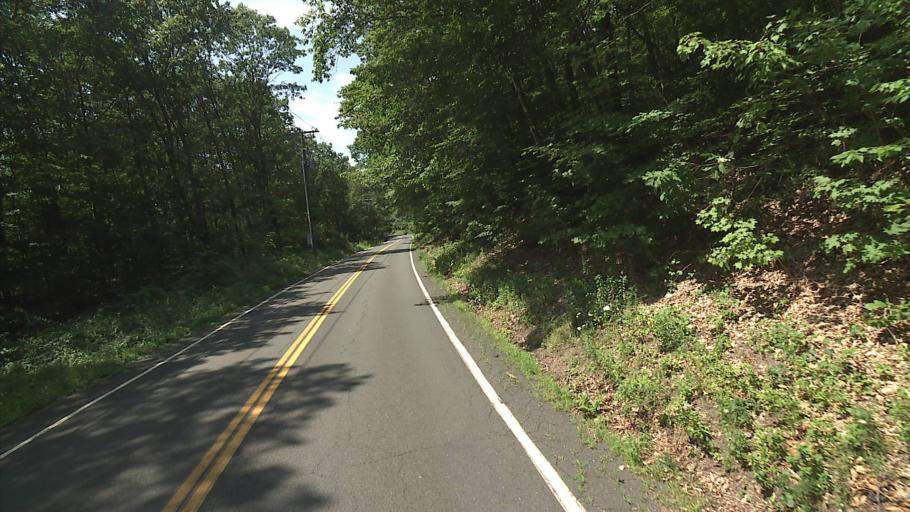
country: US
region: Connecticut
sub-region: Litchfield County
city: Winchester Center
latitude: 41.9895
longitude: -73.1562
